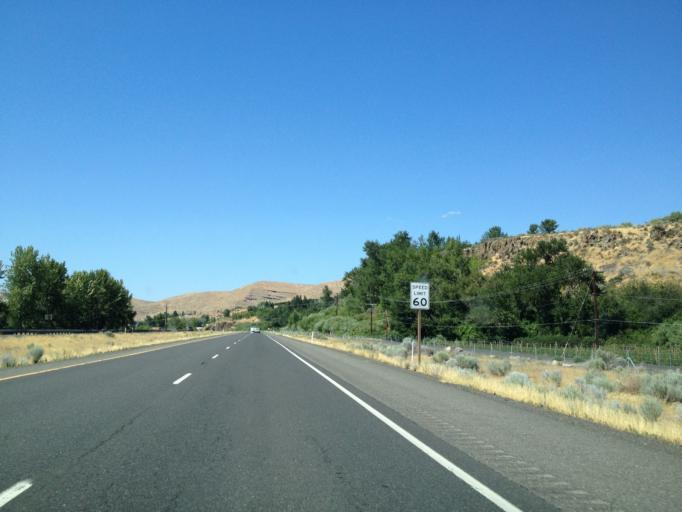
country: US
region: Washington
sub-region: Yakima County
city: Gleed
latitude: 46.6884
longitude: -120.6530
